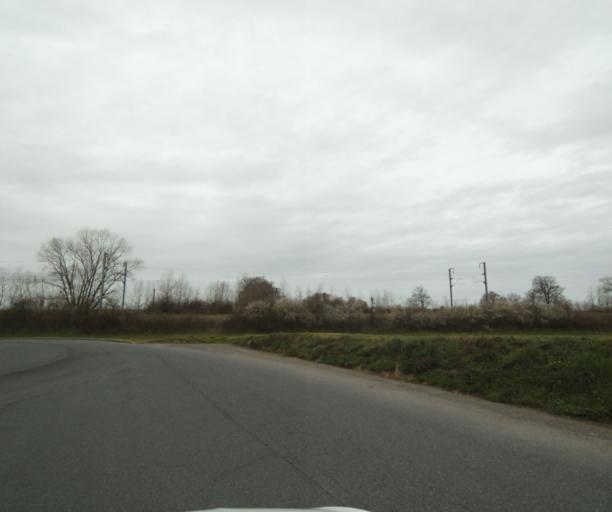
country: FR
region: Auvergne
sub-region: Departement de l'Allier
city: Toulon-sur-Allier
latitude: 46.5083
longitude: 3.3604
